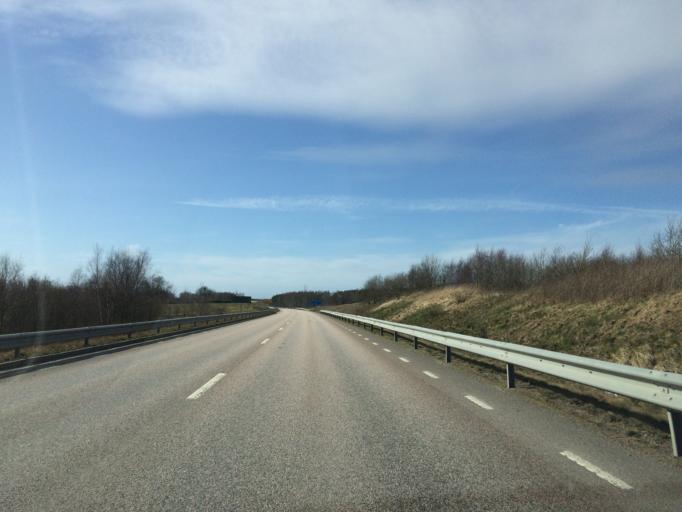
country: SE
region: Halland
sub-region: Laholms Kommun
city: Veinge
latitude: 56.5438
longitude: 13.0796
